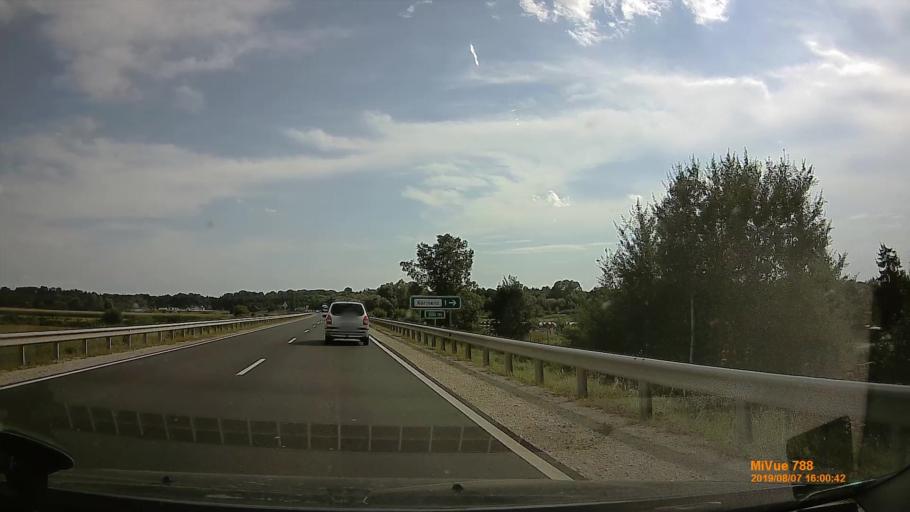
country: HU
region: Vas
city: Kormend
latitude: 46.9985
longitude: 16.6154
